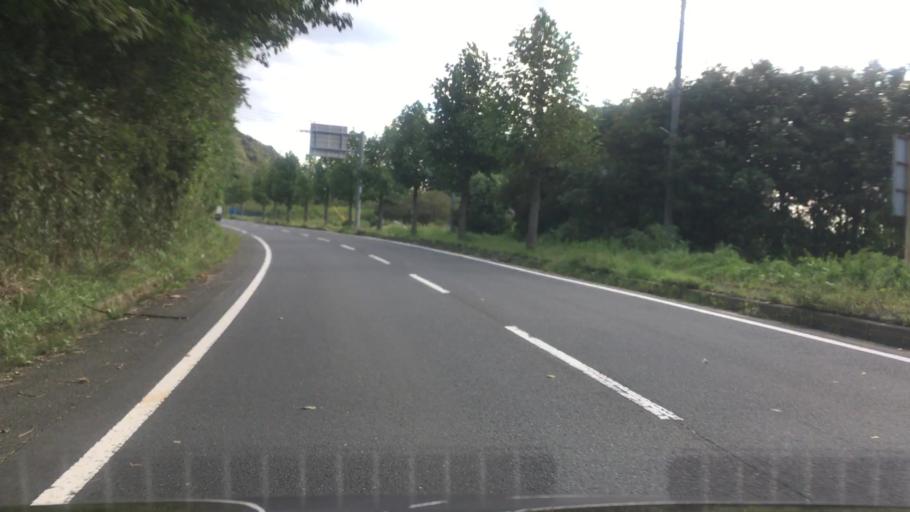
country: JP
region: Hyogo
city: Toyooka
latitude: 35.6253
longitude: 134.9285
